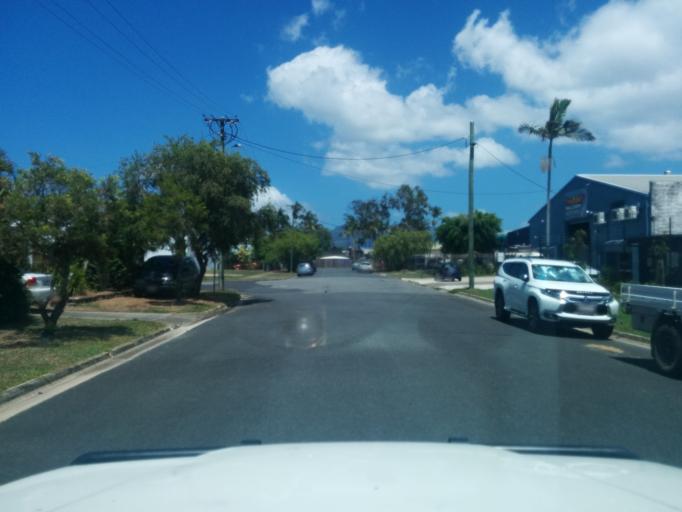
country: AU
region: Queensland
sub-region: Cairns
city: Cairns
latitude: -16.9141
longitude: 145.7459
